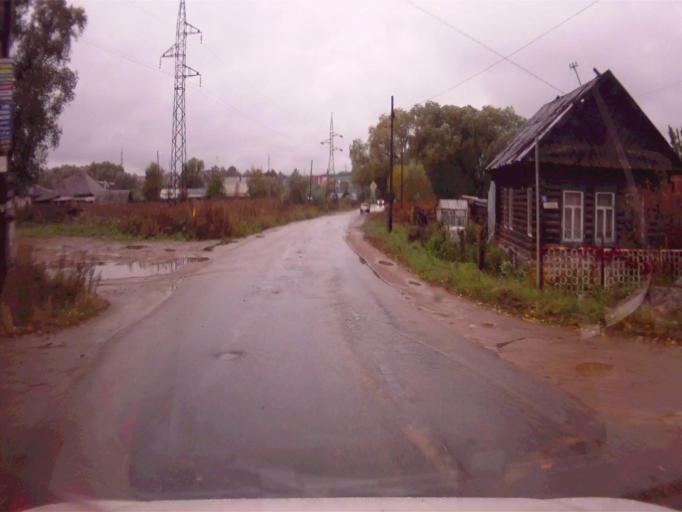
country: RU
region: Chelyabinsk
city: Kyshtym
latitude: 55.7150
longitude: 60.5471
